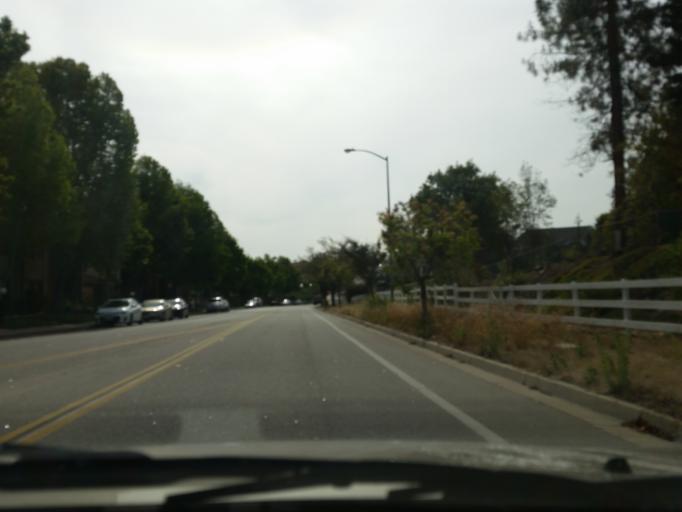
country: US
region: California
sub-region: San Luis Obispo County
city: Arroyo Grande
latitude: 35.1332
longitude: -120.6009
